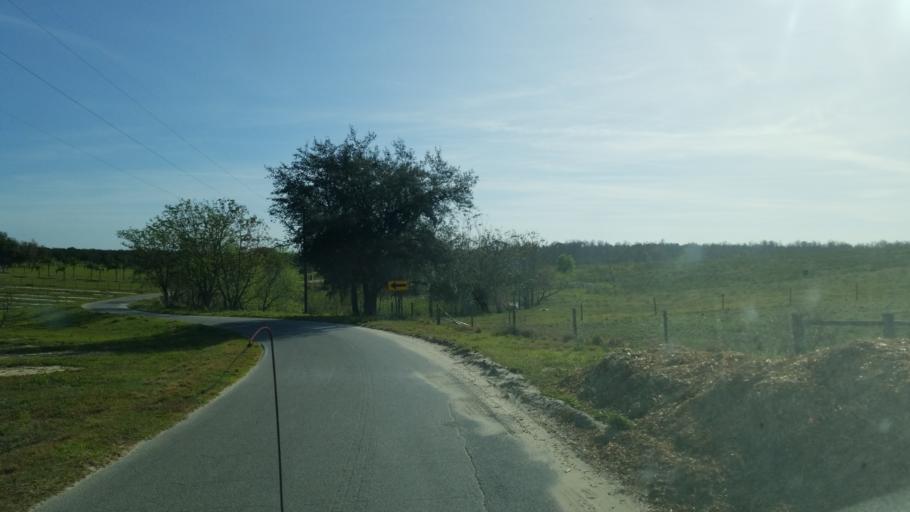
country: US
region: Florida
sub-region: Lake County
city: Clermont
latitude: 28.4614
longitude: -81.7649
